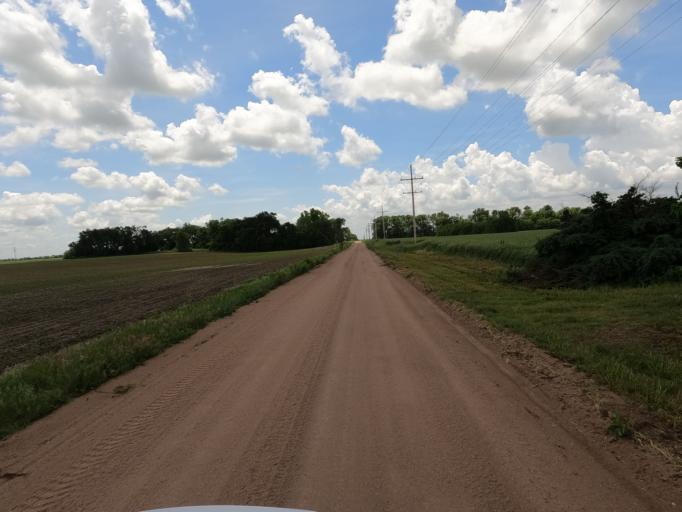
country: US
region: Kansas
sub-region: Reno County
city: Haven
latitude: 37.9008
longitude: -97.8851
